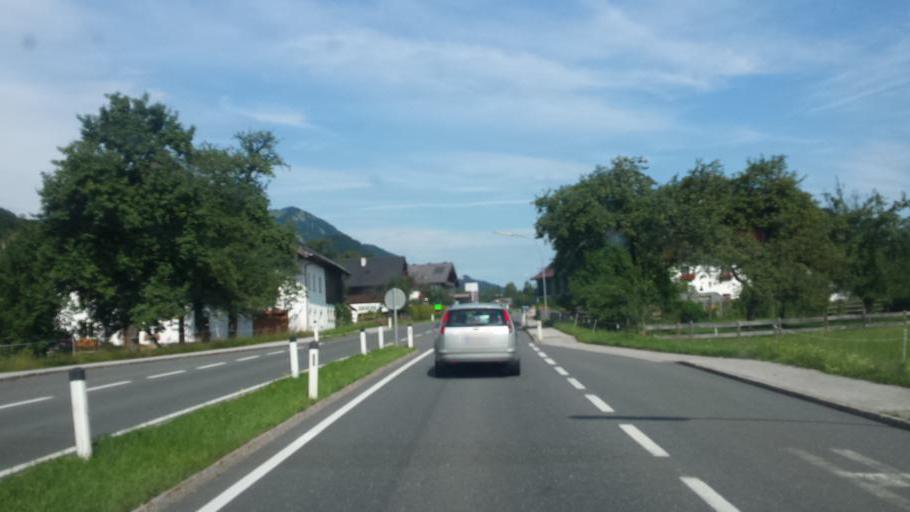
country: AT
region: Upper Austria
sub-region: Politischer Bezirk Gmunden
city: Sankt Wolfgang im Salzkammergut
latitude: 47.7223
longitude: 13.4267
